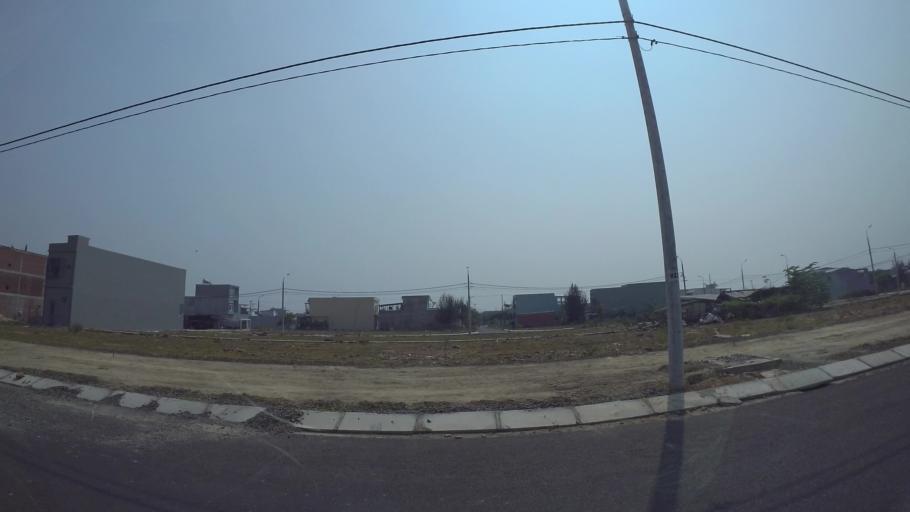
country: VN
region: Da Nang
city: Cam Le
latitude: 15.9840
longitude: 108.2275
